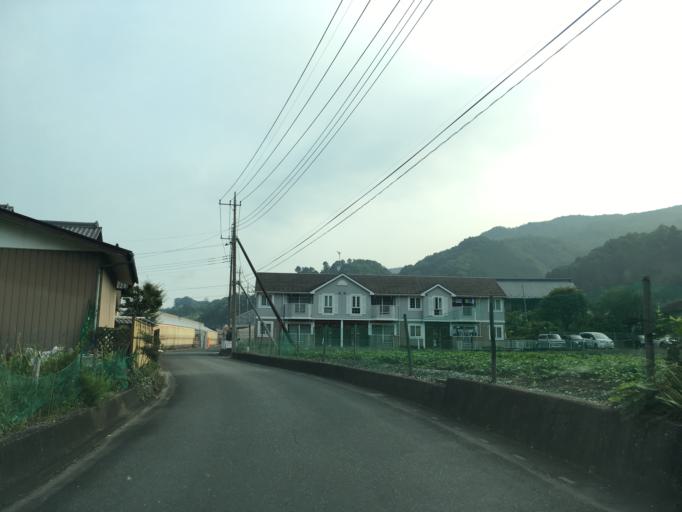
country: JP
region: Saitama
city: Chichibu
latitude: 35.9797
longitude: 139.1128
